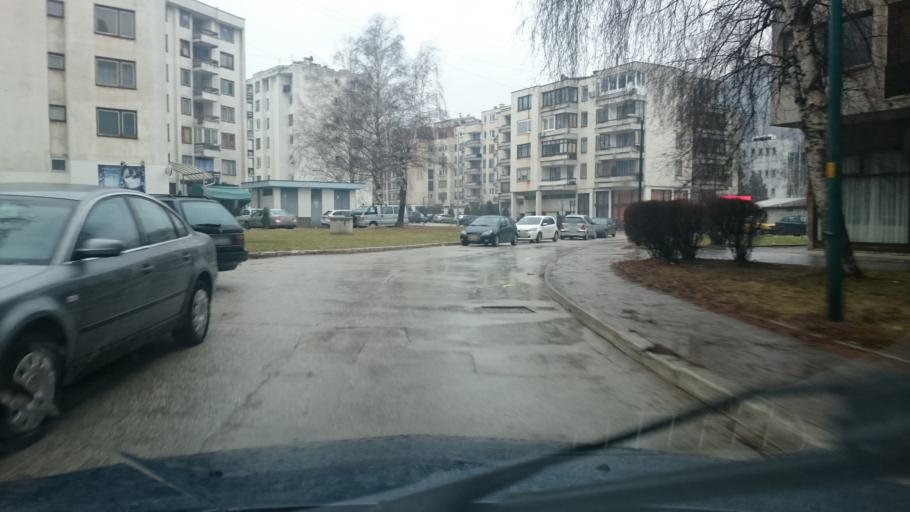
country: BA
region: Federation of Bosnia and Herzegovina
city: Travnik
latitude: 44.2246
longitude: 17.6666
